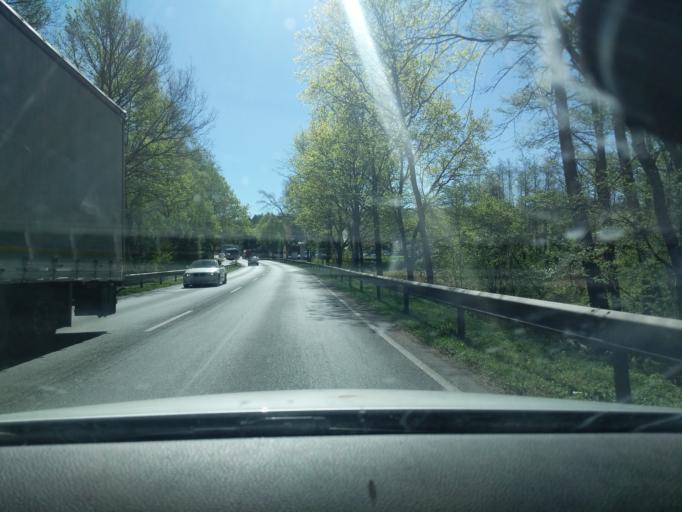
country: DE
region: Lower Saxony
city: Nottensdorf
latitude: 53.4850
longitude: 9.6187
